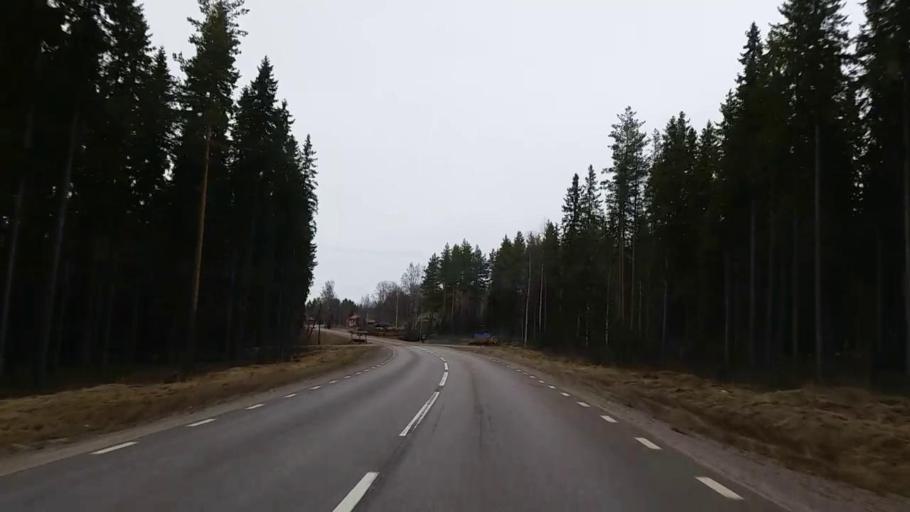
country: SE
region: Gaevleborg
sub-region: Ovanakers Kommun
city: Edsbyn
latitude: 61.2010
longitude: 15.8736
